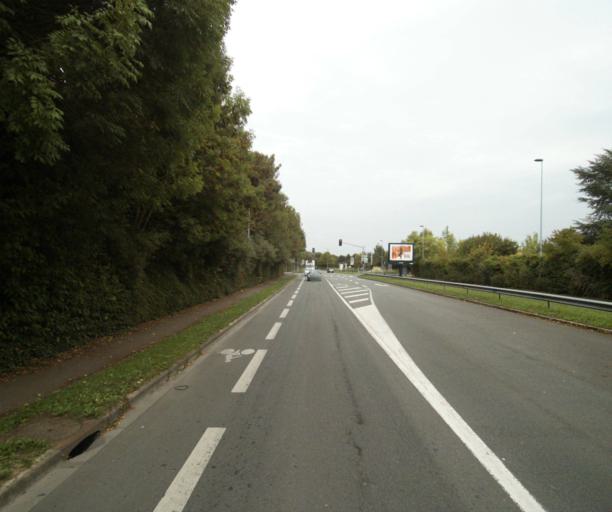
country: FR
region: Nord-Pas-de-Calais
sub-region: Departement du Nord
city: Lambersart
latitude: 50.6610
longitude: 3.0343
